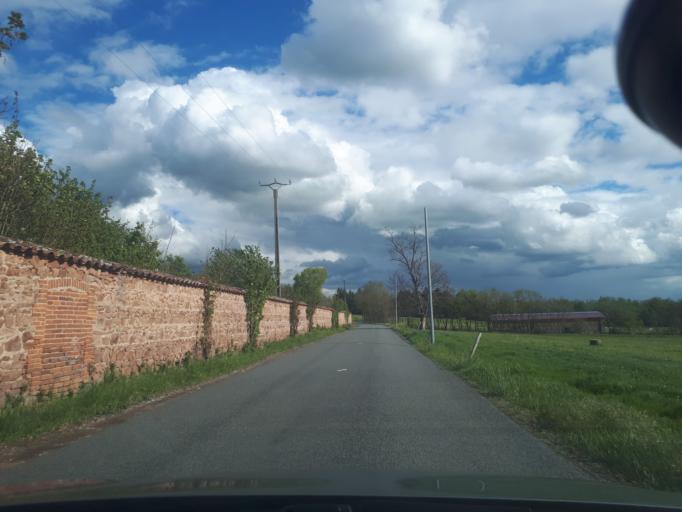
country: FR
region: Rhone-Alpes
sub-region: Departement de la Loire
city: Civens
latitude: 45.7673
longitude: 4.2628
